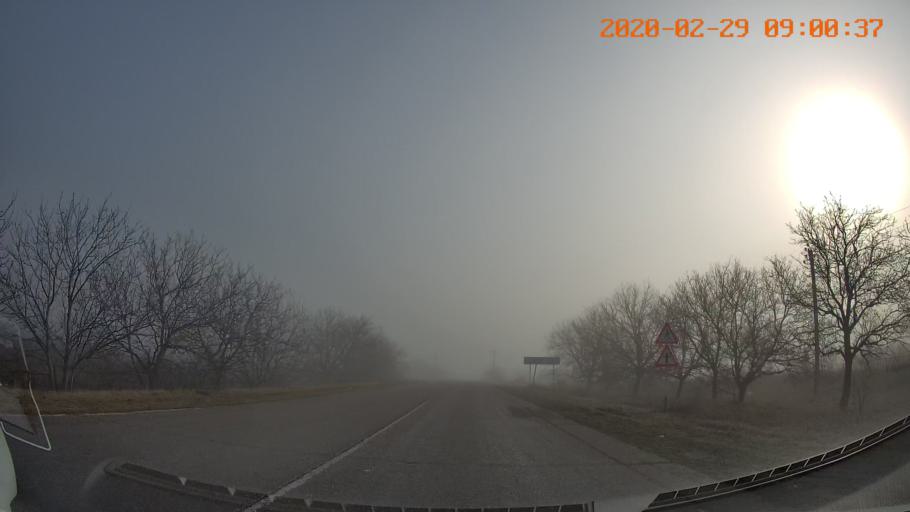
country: UA
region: Odessa
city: Velykoploske
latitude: 46.9226
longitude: 29.6798
